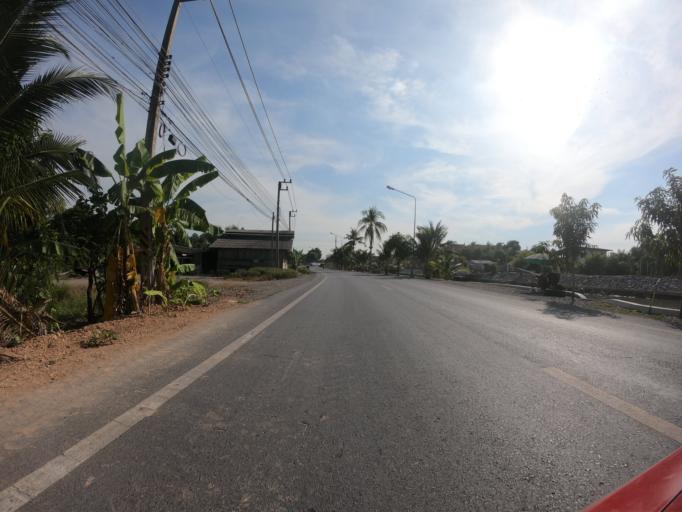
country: TH
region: Pathum Thani
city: Thanyaburi
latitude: 13.9824
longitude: 100.7293
